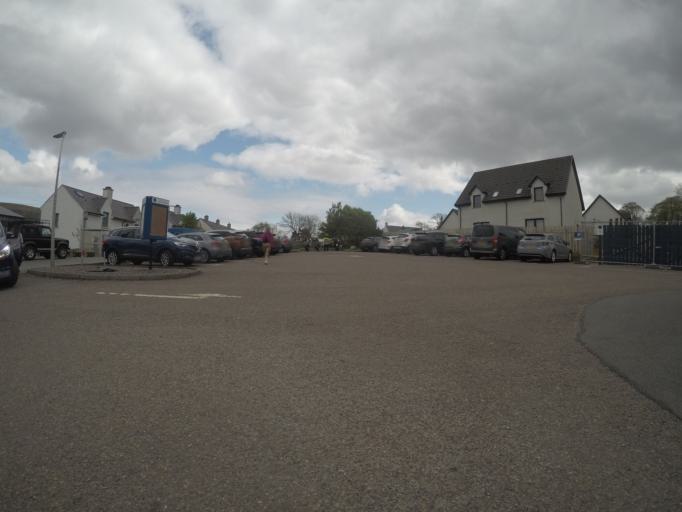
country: GB
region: Scotland
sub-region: Highland
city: Isle of Skye
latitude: 57.3025
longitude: -6.3550
